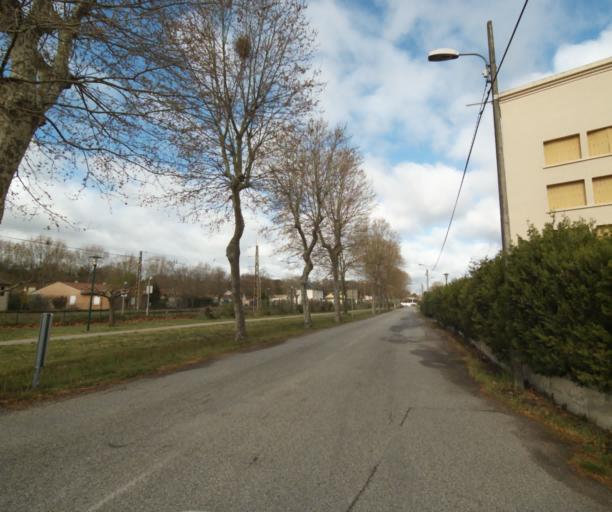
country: FR
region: Midi-Pyrenees
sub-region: Departement de l'Ariege
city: Saverdun
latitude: 43.2393
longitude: 1.5726
